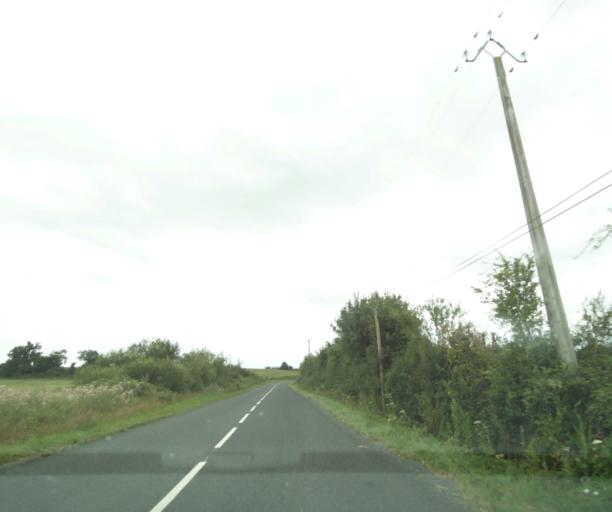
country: FR
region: Pays de la Loire
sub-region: Departement de Maine-et-Loire
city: Durtal
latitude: 47.7264
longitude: -0.2628
